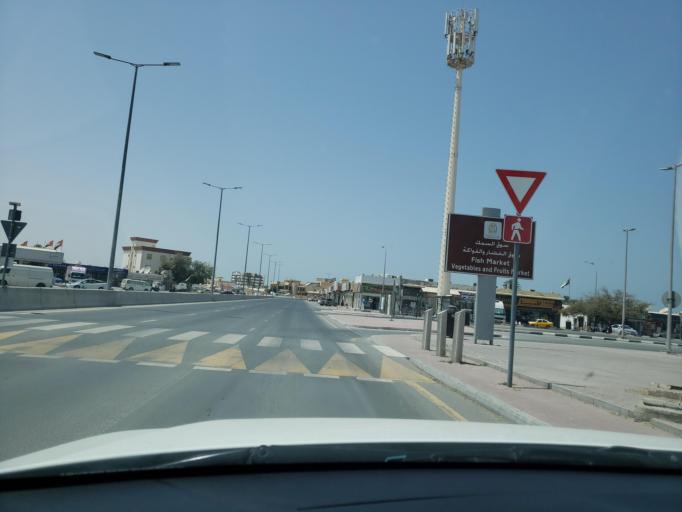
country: AE
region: Ra's al Khaymah
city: Ras al-Khaimah
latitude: 25.8165
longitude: 55.9693
